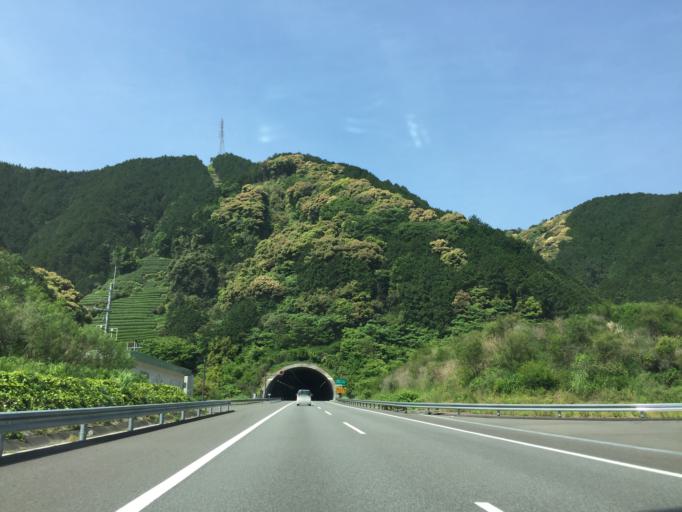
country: JP
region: Shizuoka
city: Shizuoka-shi
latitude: 35.0182
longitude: 138.3407
